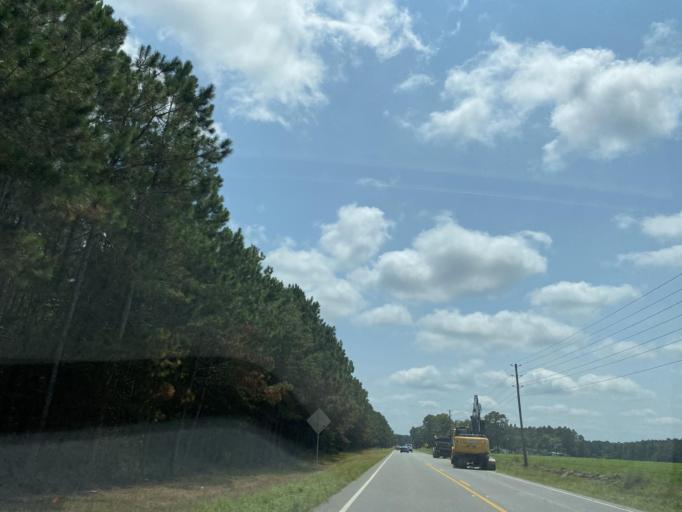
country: US
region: Georgia
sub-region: Jeff Davis County
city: Hazlehurst
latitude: 31.8034
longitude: -82.5655
